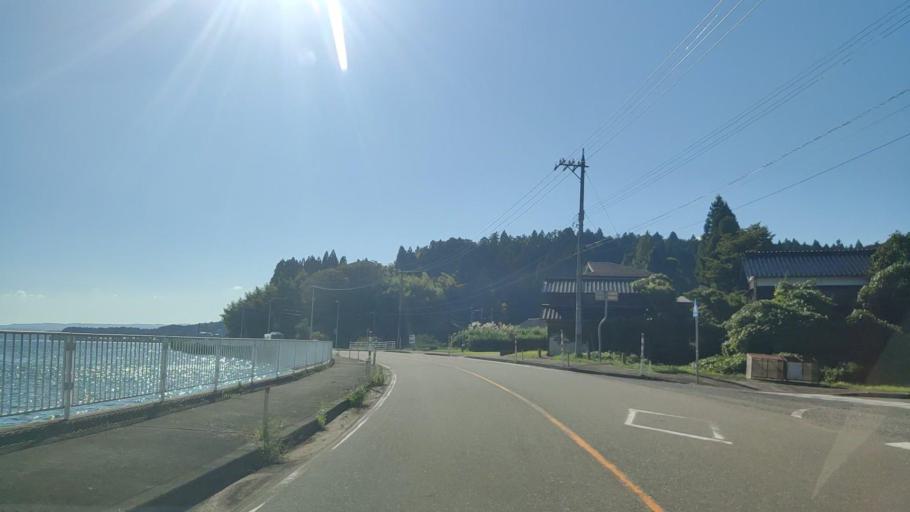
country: JP
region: Ishikawa
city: Nanao
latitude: 37.2367
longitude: 136.9605
